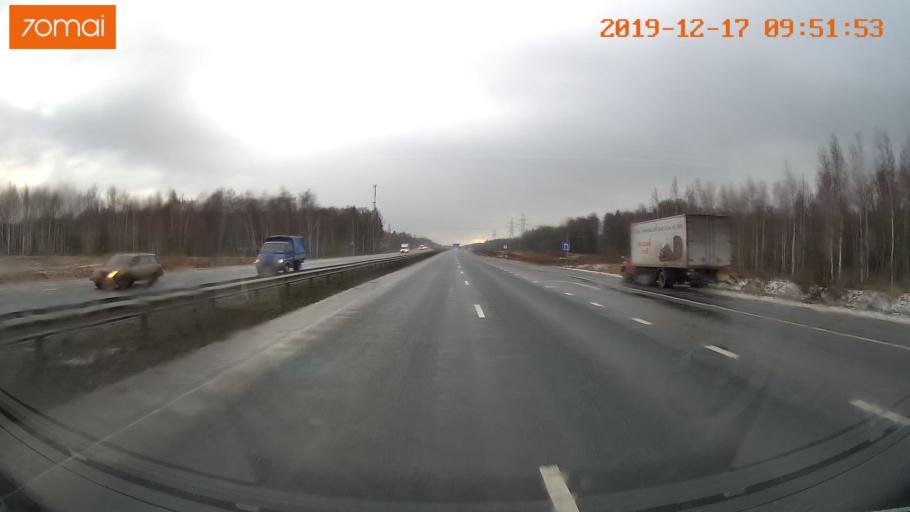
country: RU
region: Vladimir
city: Kommunar
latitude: 56.0390
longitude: 40.5281
